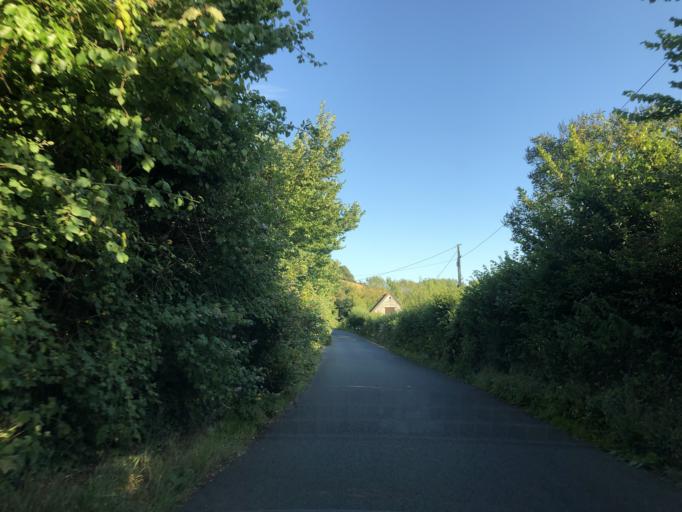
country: GB
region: England
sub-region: Isle of Wight
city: Shalfleet
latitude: 50.6527
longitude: -1.3999
